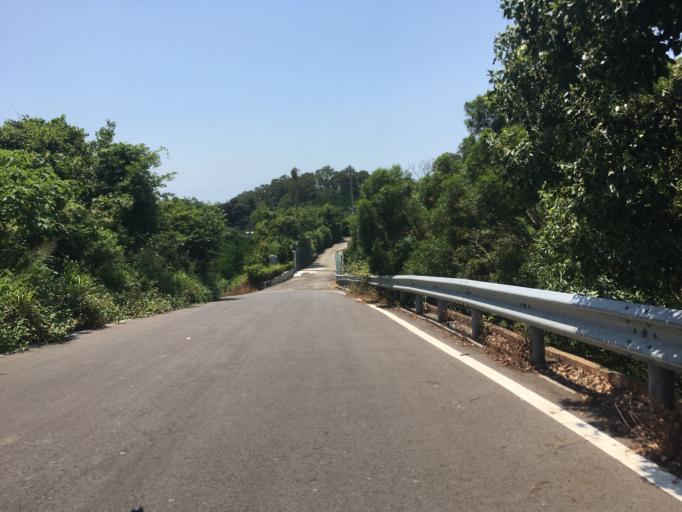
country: TW
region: Taiwan
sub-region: Hsinchu
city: Hsinchu
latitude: 24.7325
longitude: 120.9857
